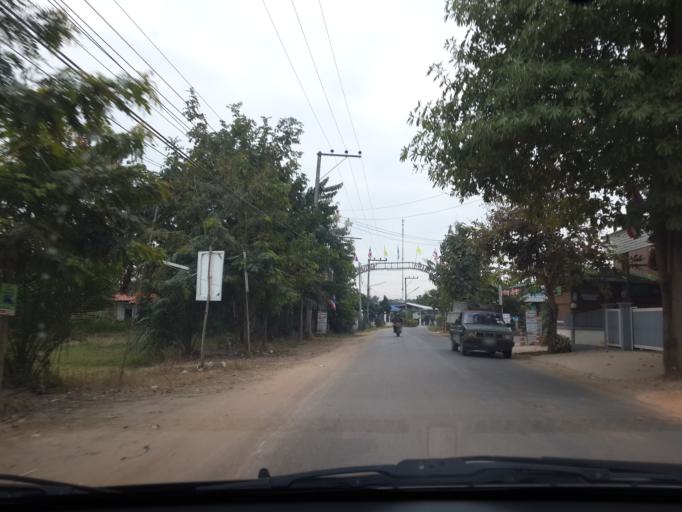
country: TH
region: Chiang Mai
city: San Sai
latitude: 18.8944
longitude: 99.0951
